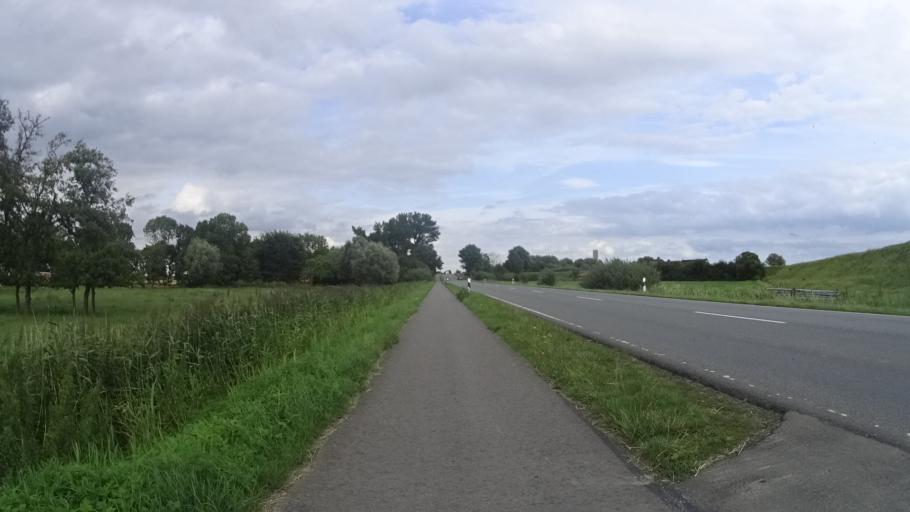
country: DE
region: Lower Saxony
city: Wischhafen
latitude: 53.7843
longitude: 9.3303
